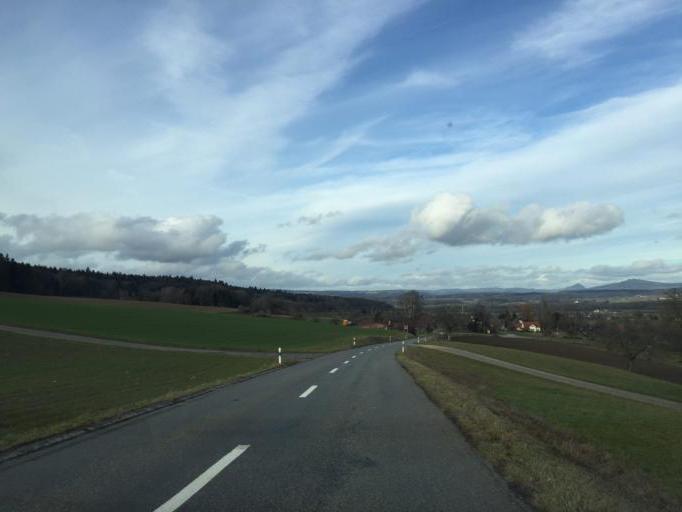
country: DE
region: Baden-Wuerttemberg
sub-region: Freiburg Region
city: Busingen
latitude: 47.6538
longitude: 8.6904
